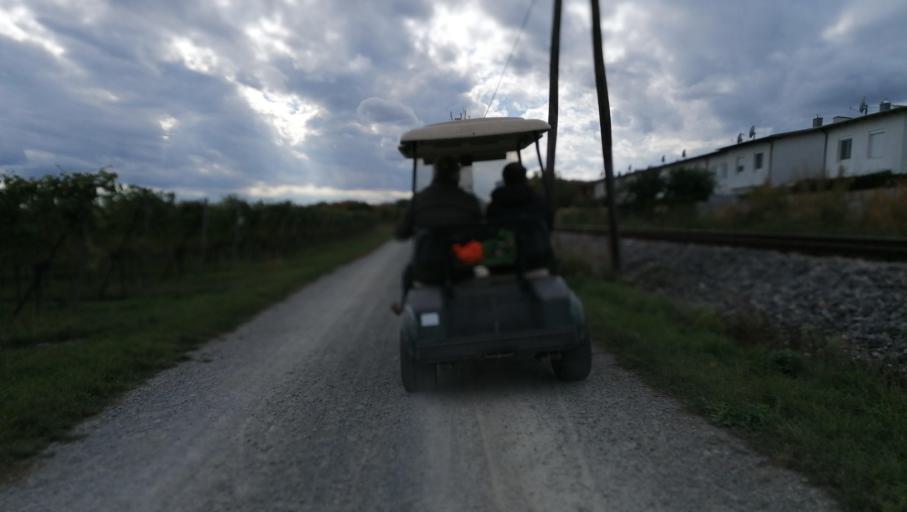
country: AT
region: Lower Austria
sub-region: Politischer Bezirk Baden
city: Tattendorf
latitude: 47.9600
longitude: 16.3116
